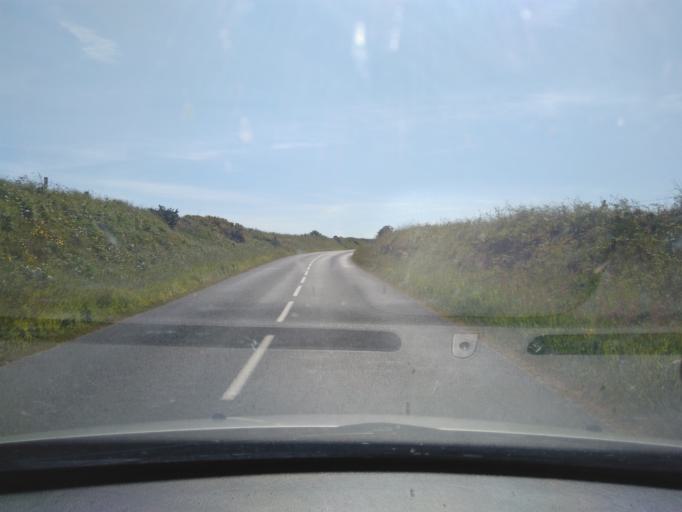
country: FR
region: Lower Normandy
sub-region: Departement de la Manche
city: Beaumont-Hague
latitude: 49.6973
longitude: -1.9245
